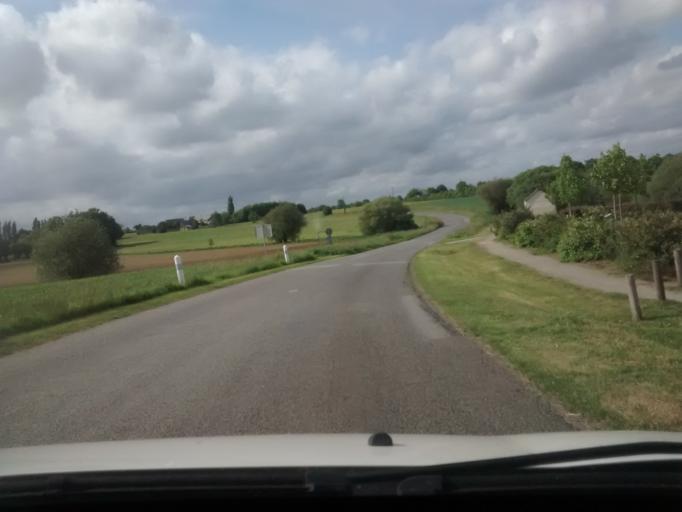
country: FR
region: Brittany
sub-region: Departement d'Ille-et-Vilaine
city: Nouvoitou
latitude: 48.0655
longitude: -1.5285
